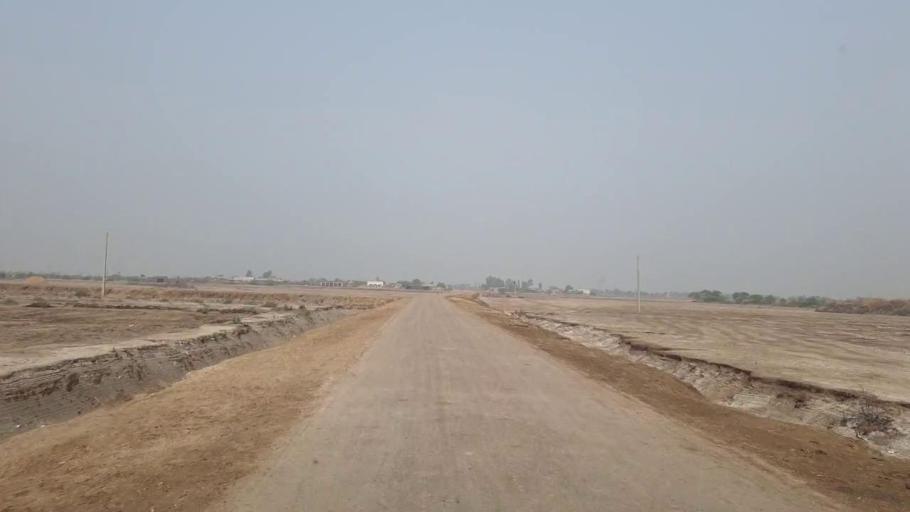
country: PK
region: Sindh
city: Kario
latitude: 24.6552
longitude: 68.6212
